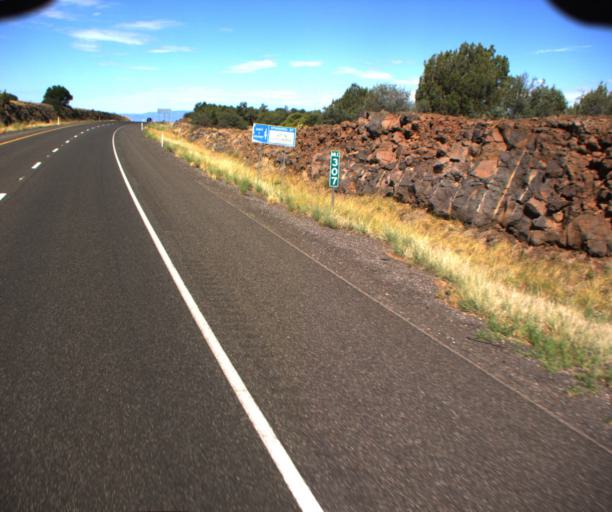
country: US
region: Arizona
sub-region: Yavapai County
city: Village of Oak Creek (Big Park)
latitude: 34.7687
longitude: -111.6455
